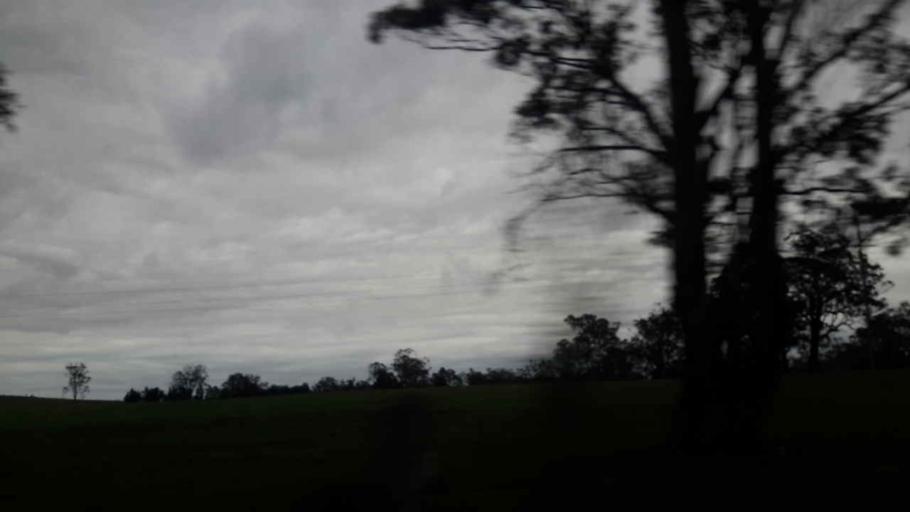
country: AU
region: New South Wales
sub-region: Wollondilly
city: Douglas Park
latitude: -34.2063
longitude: 150.7194
